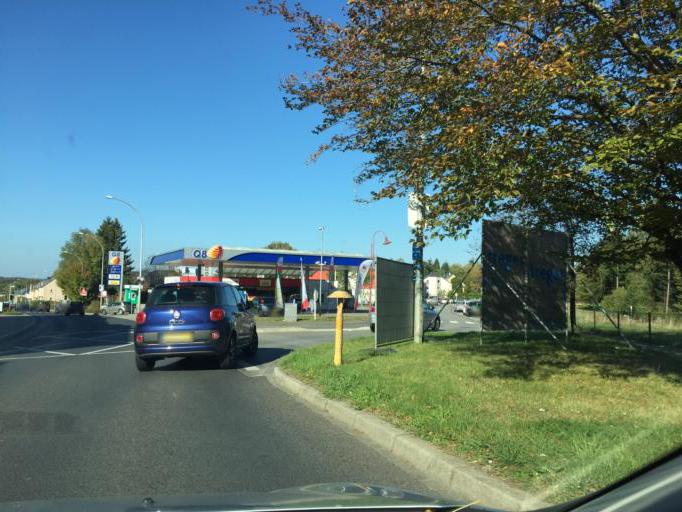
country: LU
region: Luxembourg
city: Bridel
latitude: 49.6560
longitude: 6.0832
